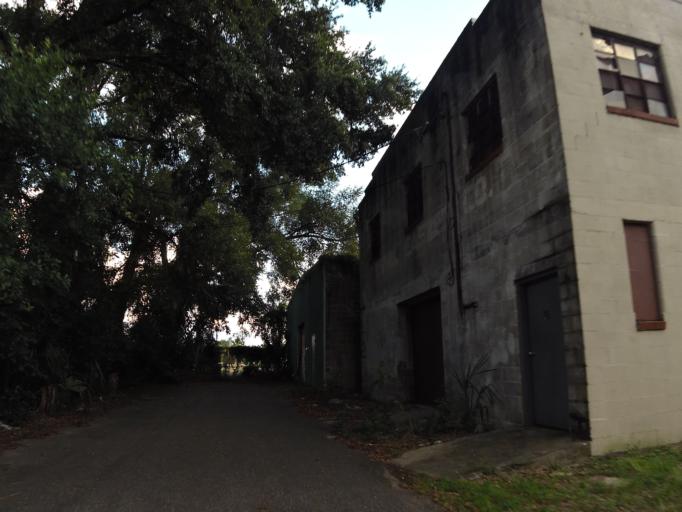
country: US
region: Florida
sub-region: Duval County
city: Jacksonville
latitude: 30.3219
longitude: -81.6864
